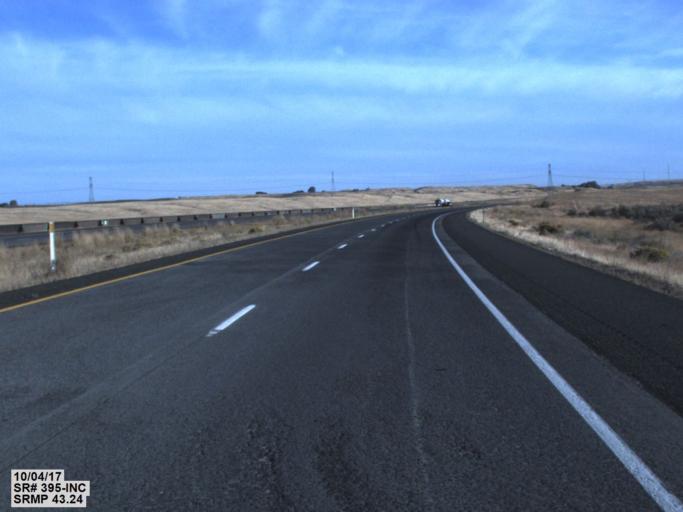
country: US
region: Washington
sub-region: Franklin County
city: Basin City
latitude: 46.5321
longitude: -119.0149
